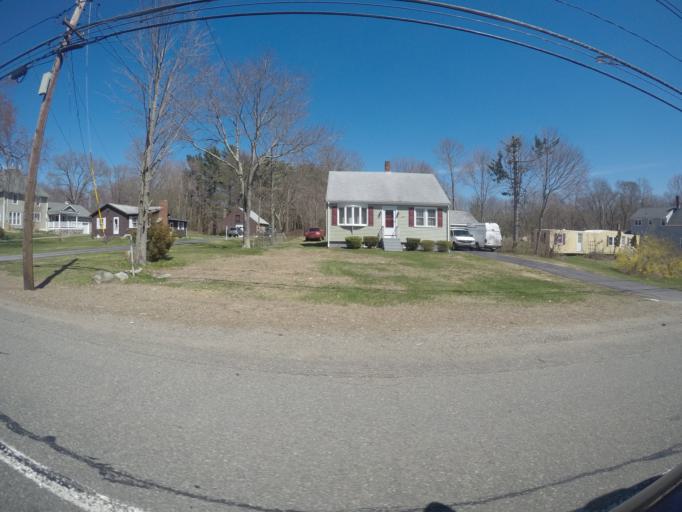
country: US
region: Massachusetts
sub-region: Norfolk County
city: Stoughton
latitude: 42.0733
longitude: -71.0876
